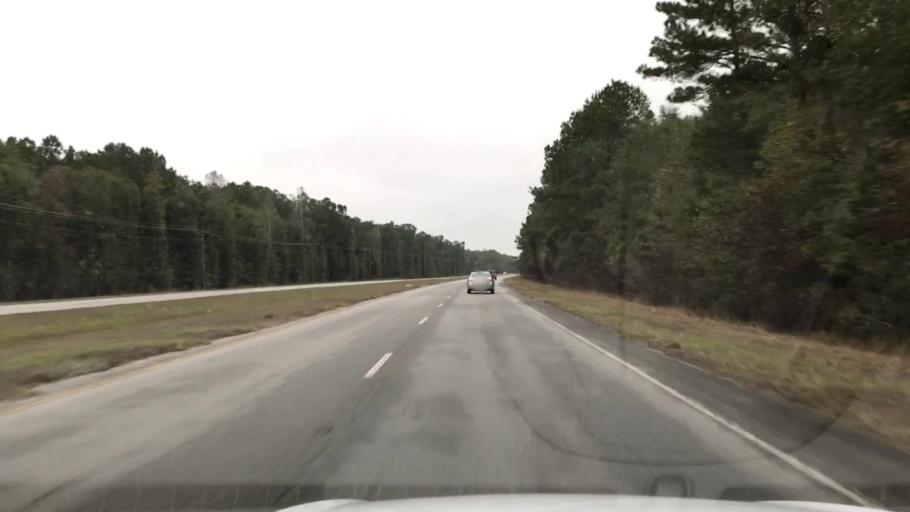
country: US
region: South Carolina
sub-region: Charleston County
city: Awendaw
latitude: 32.9555
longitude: -79.6927
